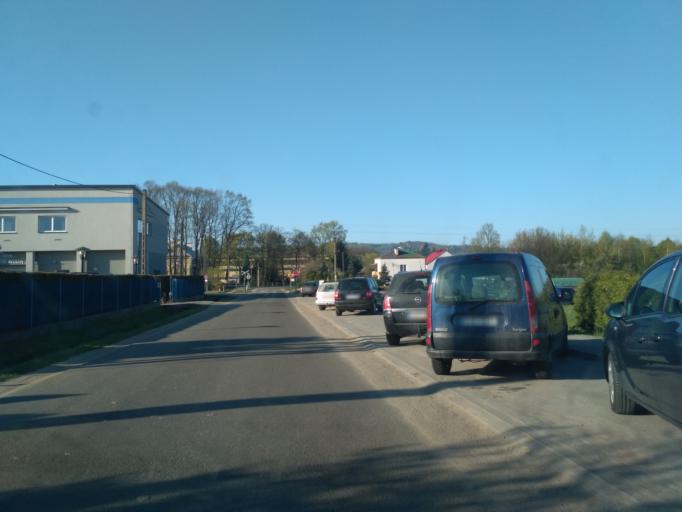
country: PL
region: Subcarpathian Voivodeship
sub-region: Powiat jasielski
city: Trzcinica
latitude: 49.7368
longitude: 21.3815
